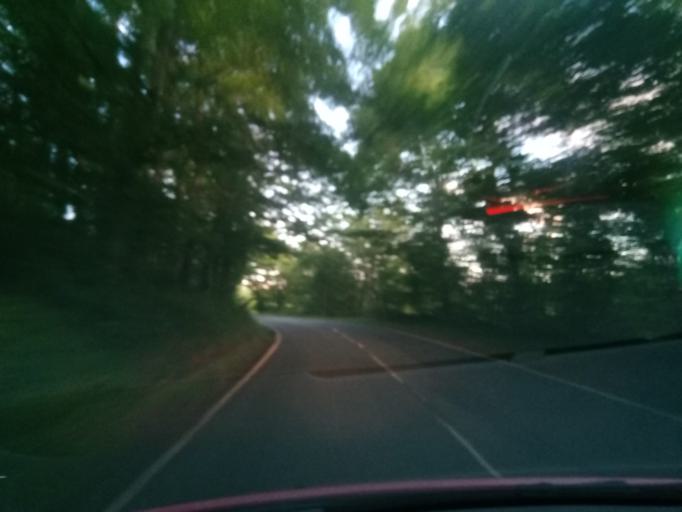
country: GB
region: England
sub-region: Northumberland
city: Bardon Mill
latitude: 54.9233
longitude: -2.3099
